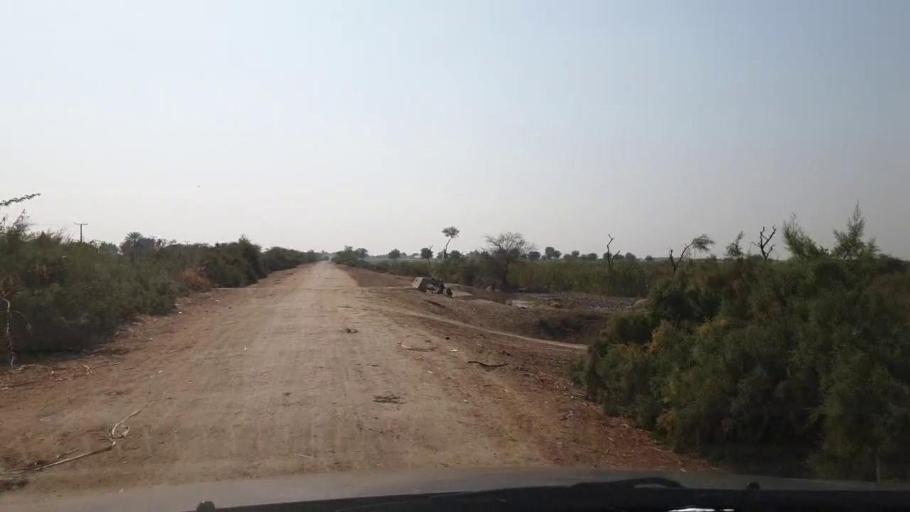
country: PK
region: Sindh
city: Jhol
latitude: 25.8472
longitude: 68.9895
